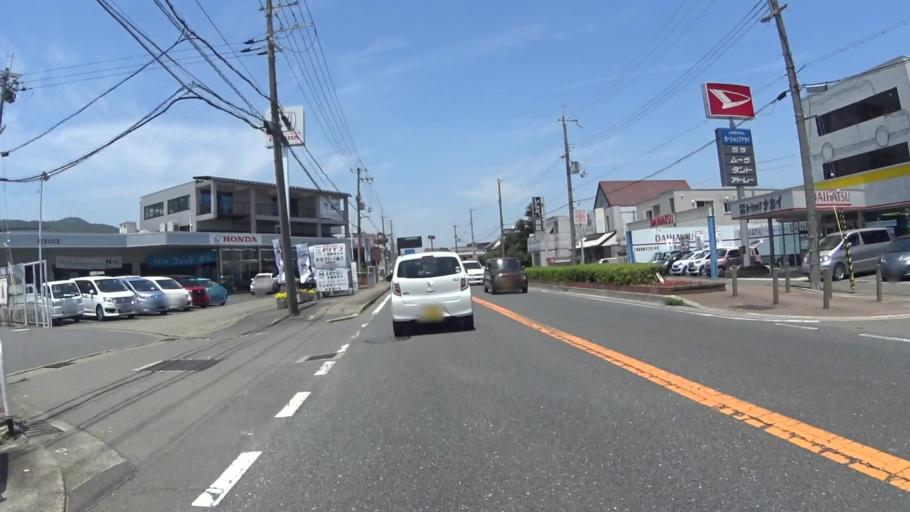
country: JP
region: Kyoto
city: Kameoka
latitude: 35.0289
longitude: 135.5546
